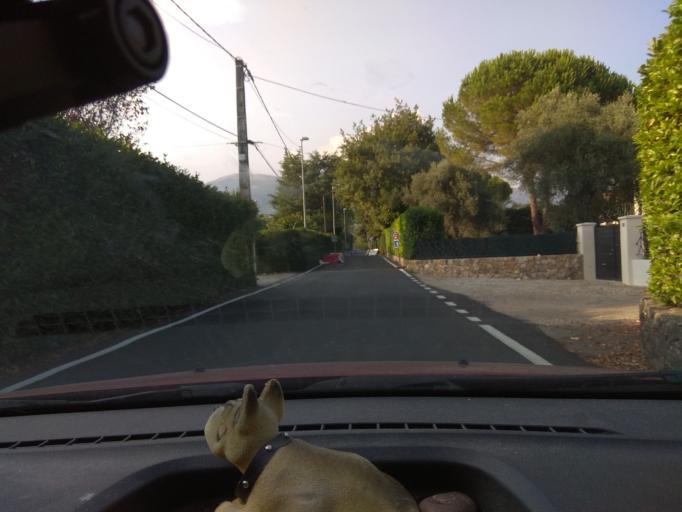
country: FR
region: Provence-Alpes-Cote d'Azur
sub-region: Departement des Alpes-Maritimes
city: Le Rouret
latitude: 43.6751
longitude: 7.0459
